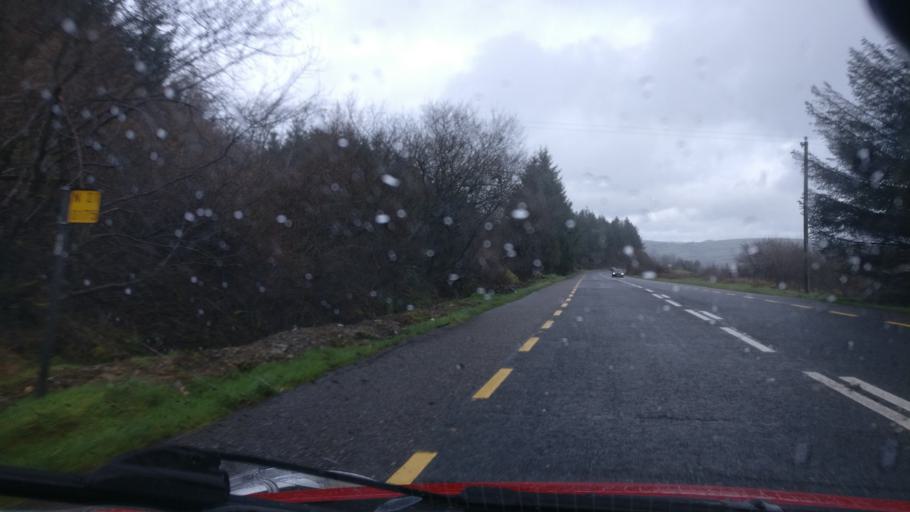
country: IE
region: Munster
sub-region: Ciarrai
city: Castleisland
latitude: 52.2968
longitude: -9.3892
